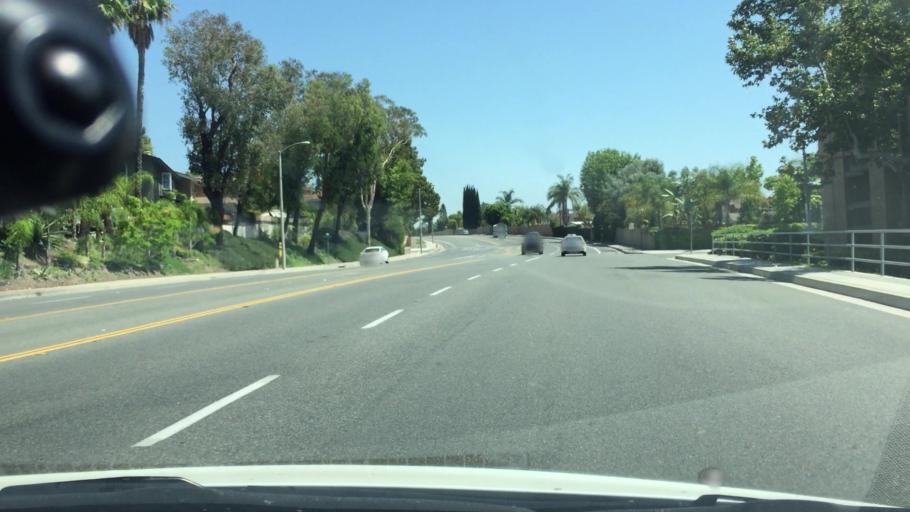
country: US
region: California
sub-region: Orange County
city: Laguna Hills
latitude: 33.6330
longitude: -117.7093
